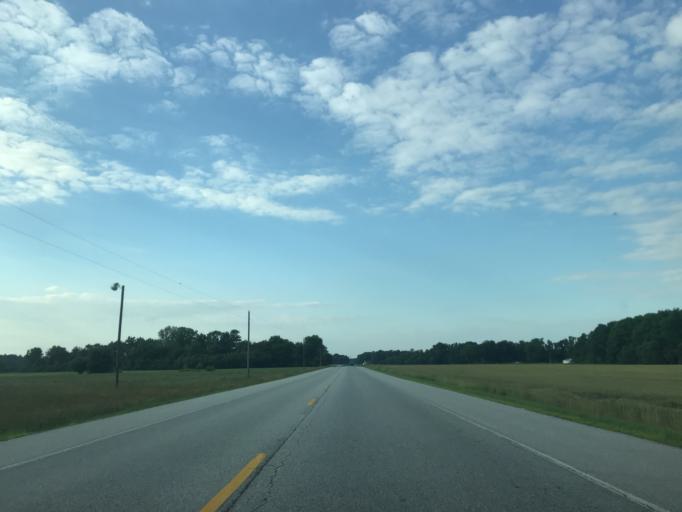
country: US
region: Maryland
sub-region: Caroline County
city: Federalsburg
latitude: 38.7670
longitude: -75.7881
